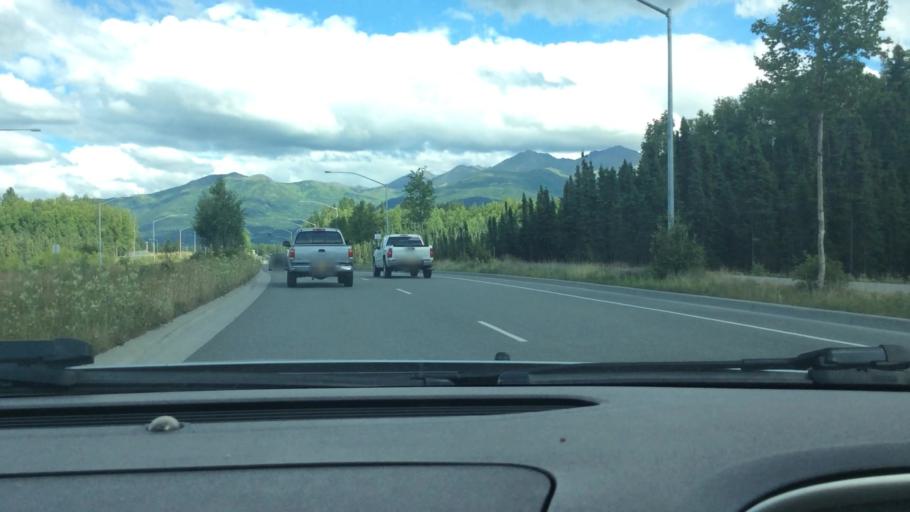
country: US
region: Alaska
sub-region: Anchorage Municipality
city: Anchorage
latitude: 61.1777
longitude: -149.7917
